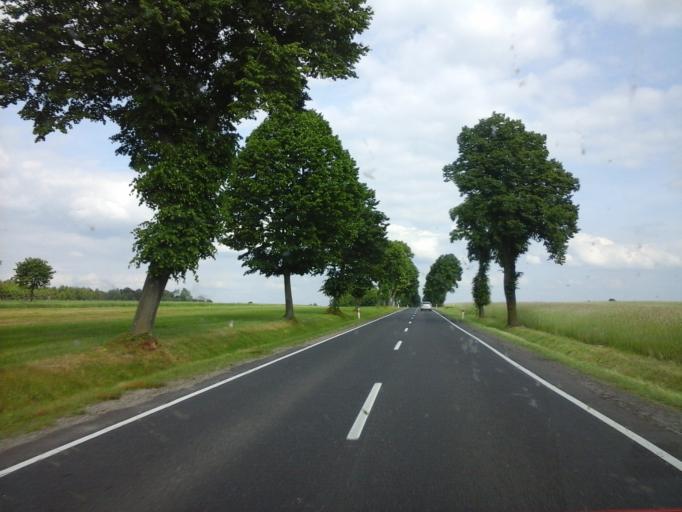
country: PL
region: Lodz Voivodeship
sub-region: Powiat opoczynski
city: Mniszkow
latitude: 51.3339
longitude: 20.0126
